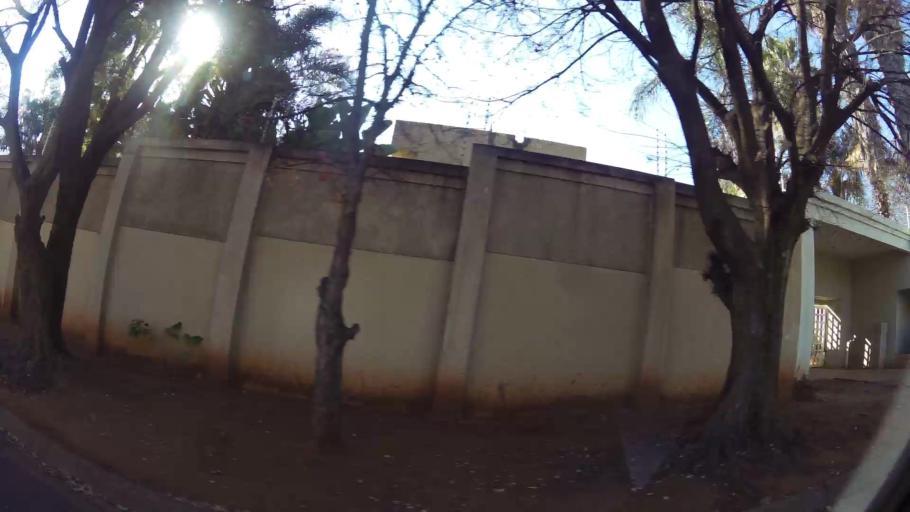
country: ZA
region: Gauteng
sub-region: Ekurhuleni Metropolitan Municipality
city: Germiston
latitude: -26.1719
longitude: 28.1536
